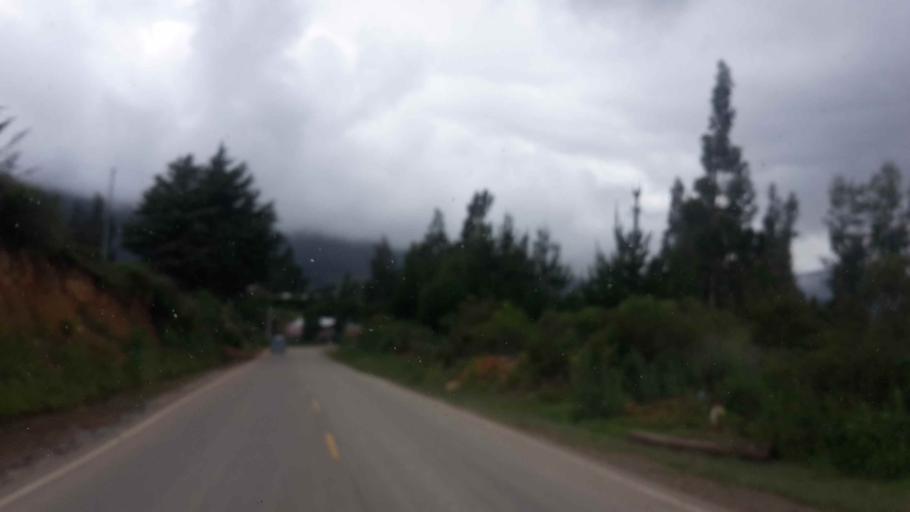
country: BO
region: Cochabamba
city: Totora
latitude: -17.5801
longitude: -65.3101
